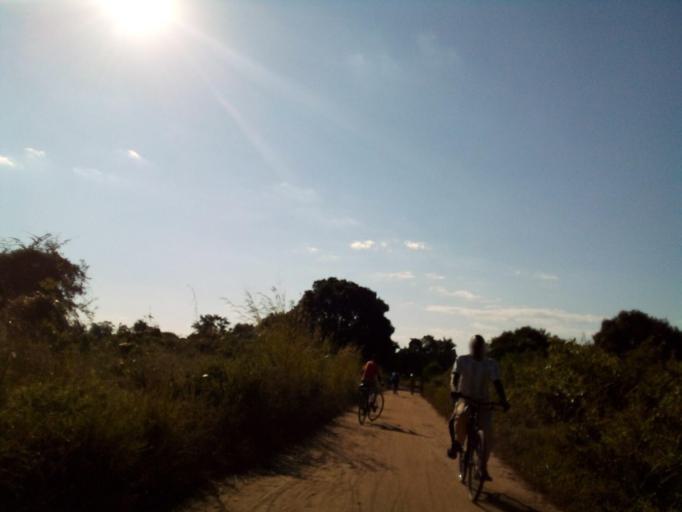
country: MZ
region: Zambezia
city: Quelimane
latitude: -17.5312
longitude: 36.6835
